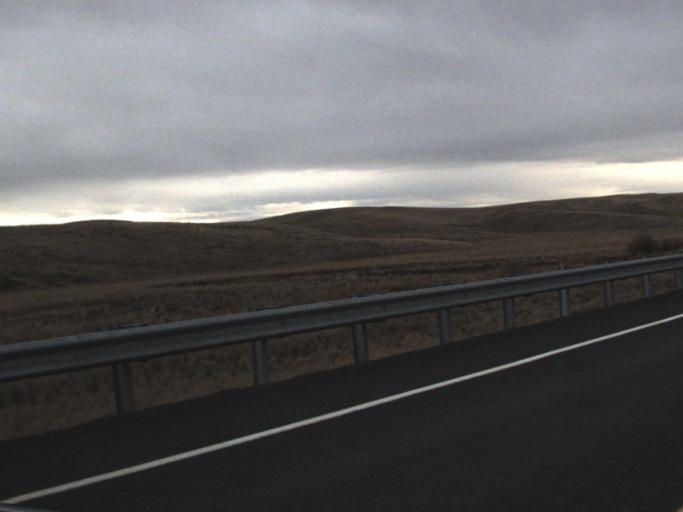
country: US
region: Washington
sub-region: Garfield County
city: Pomeroy
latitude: 46.7845
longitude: -117.9175
